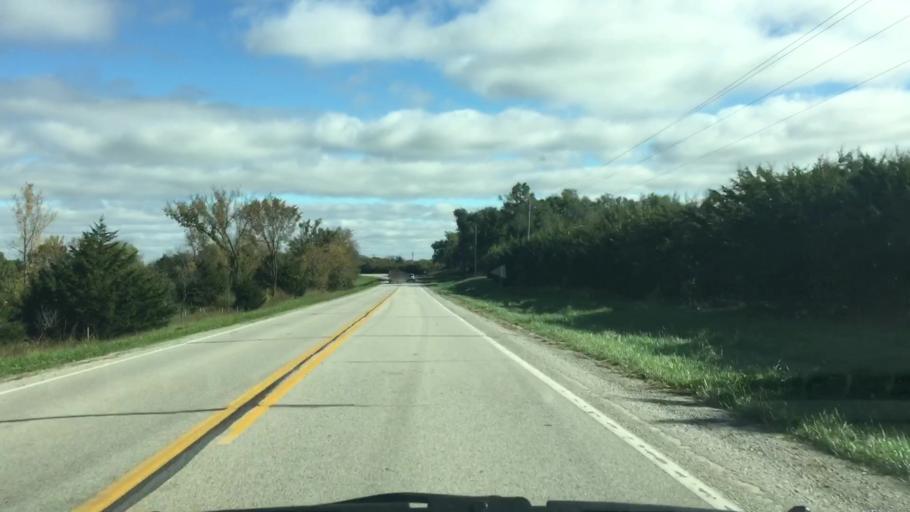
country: US
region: Iowa
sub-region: Decatur County
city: Leon
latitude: 40.7020
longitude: -93.7689
